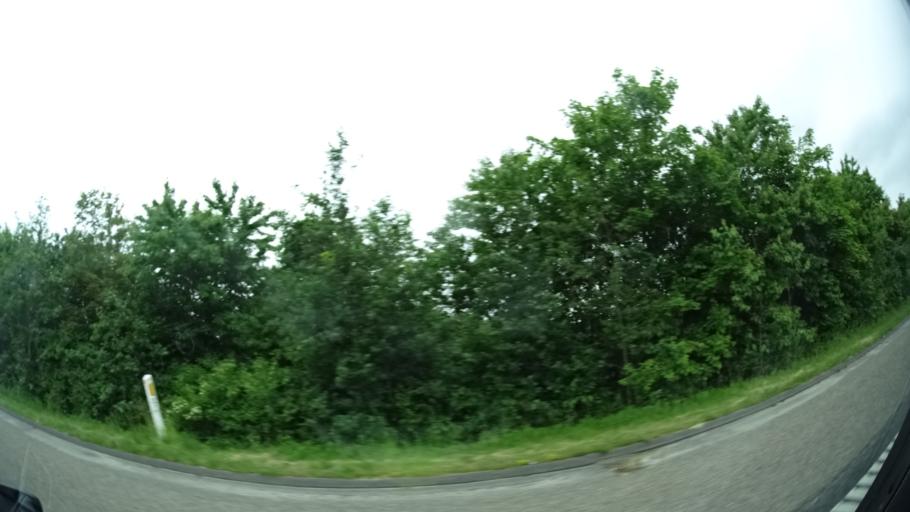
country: DK
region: Central Jutland
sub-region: Skanderborg Kommune
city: Horning
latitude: 56.1132
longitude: 10.0391
